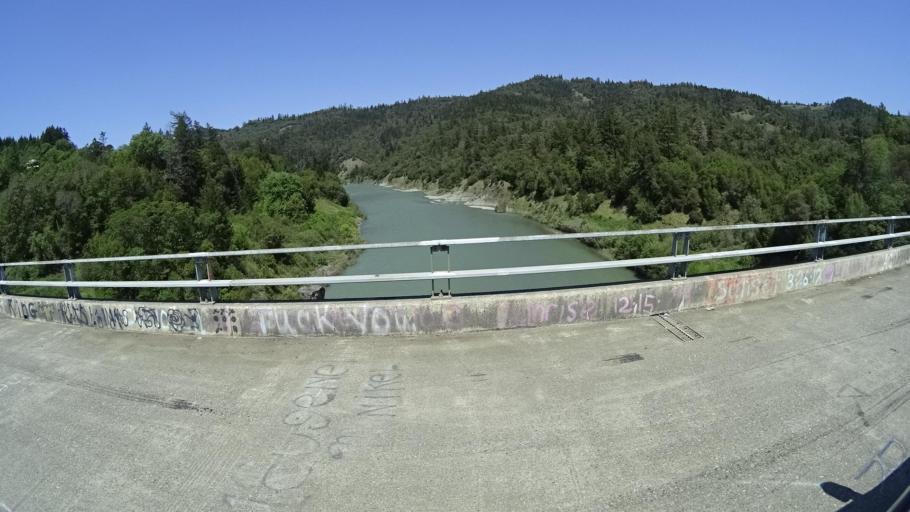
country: US
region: California
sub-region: Humboldt County
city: Redway
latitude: 40.1732
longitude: -123.6038
